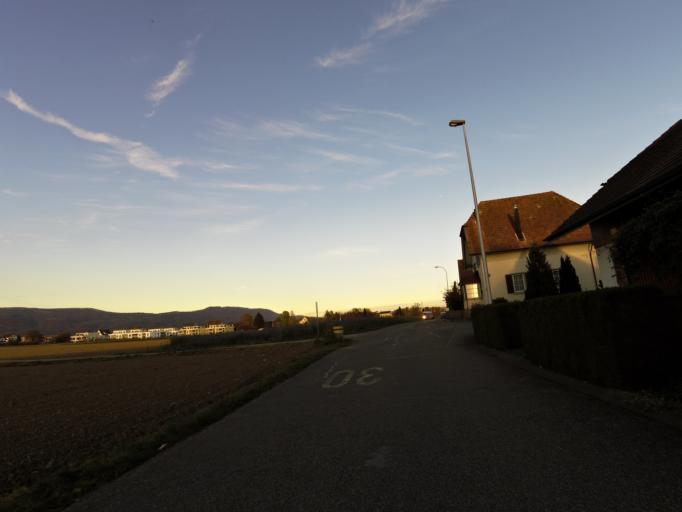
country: CH
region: Aargau
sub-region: Bezirk Aarau
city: Suhr
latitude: 47.3810
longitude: 8.0754
